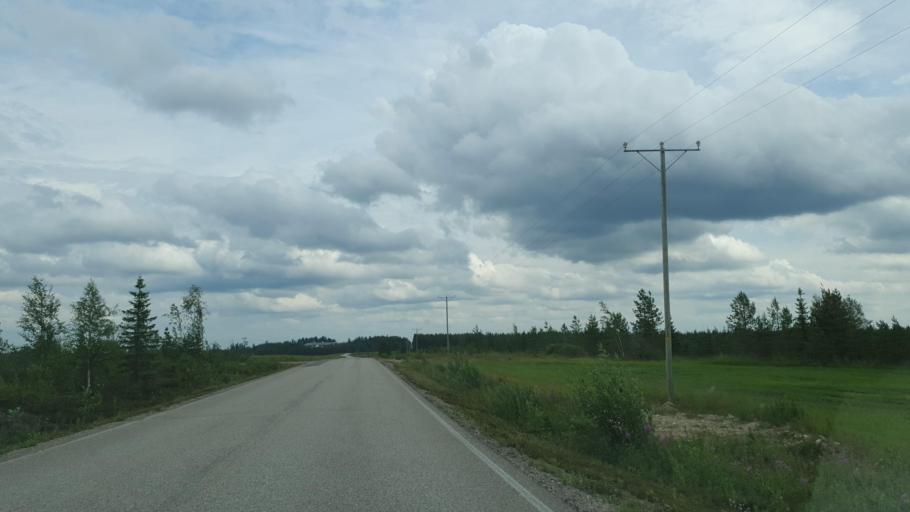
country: FI
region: Kainuu
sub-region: Kehys-Kainuu
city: Kuhmo
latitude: 64.6035
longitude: 29.7609
